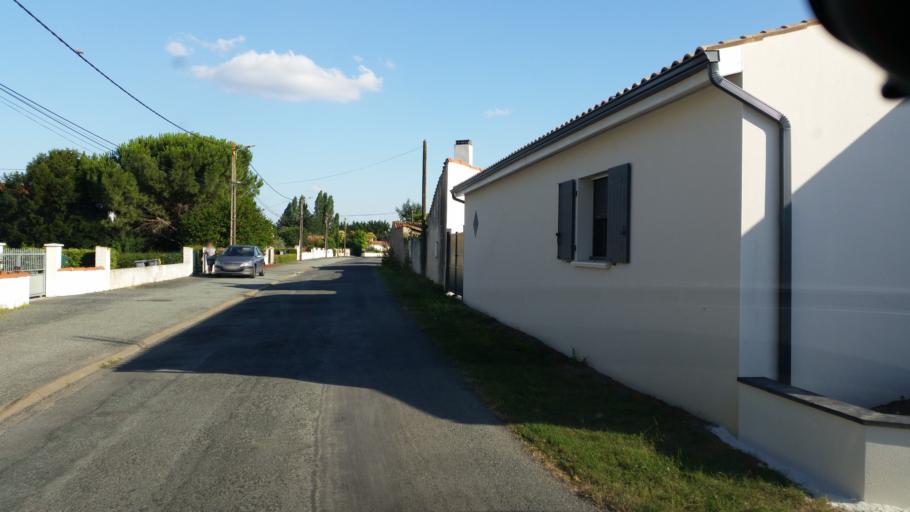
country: FR
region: Poitou-Charentes
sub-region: Departement de la Charente-Maritime
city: Marans
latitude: 46.3069
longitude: -0.9845
